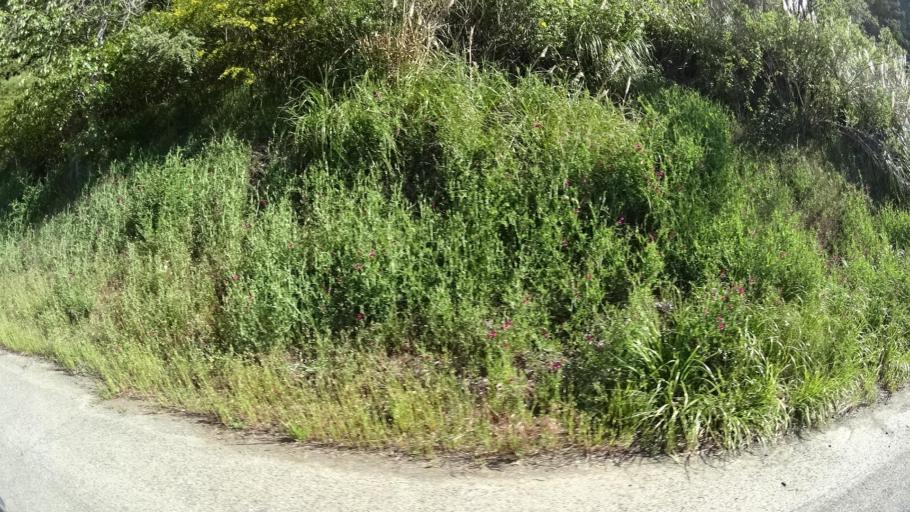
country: US
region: California
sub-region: Humboldt County
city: Rio Dell
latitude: 40.4587
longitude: -124.0691
